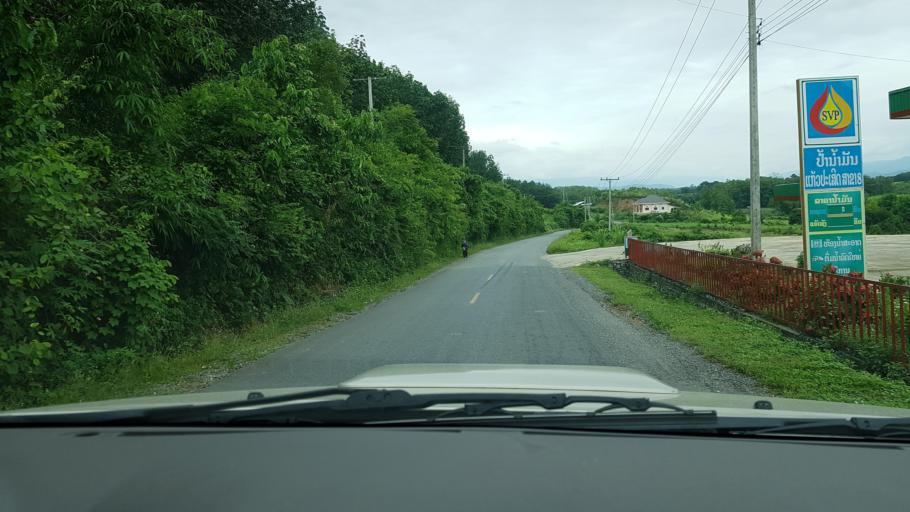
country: LA
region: Loungnamtha
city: Muang Nale
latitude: 20.1643
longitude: 101.5071
